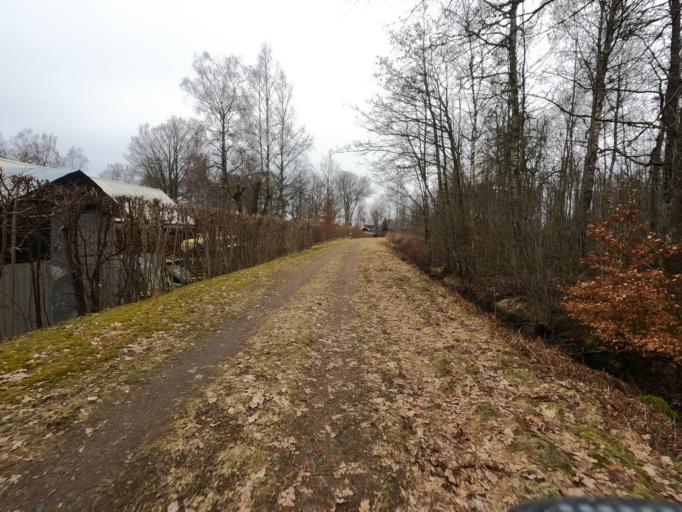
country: SE
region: Kronoberg
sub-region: Ljungby Kommun
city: Ljungby
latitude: 56.8125
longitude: 13.6909
